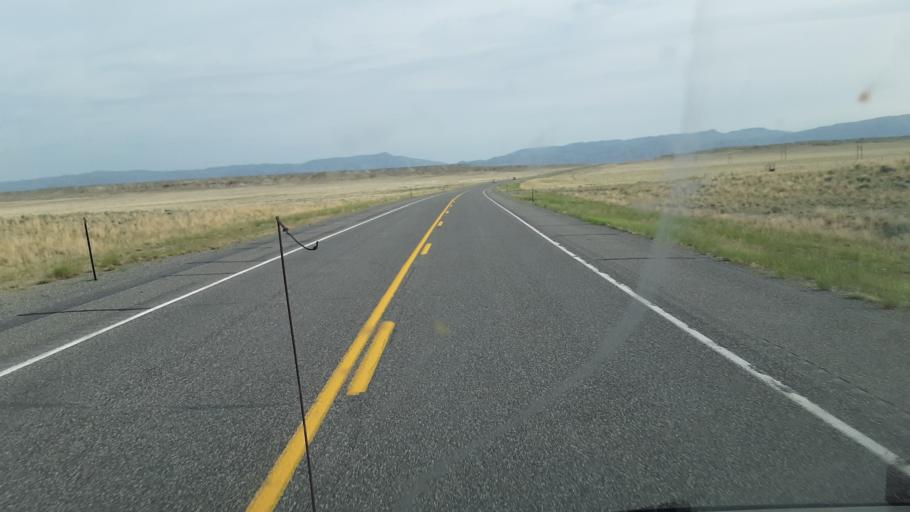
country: US
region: Wyoming
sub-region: Hot Springs County
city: Thermopolis
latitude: 43.2923
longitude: -108.1282
